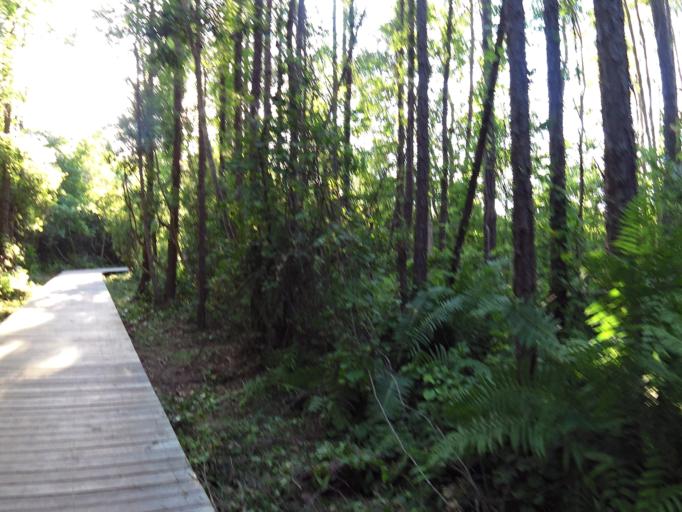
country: US
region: Florida
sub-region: Duval County
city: Atlantic Beach
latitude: 30.3834
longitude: -81.4938
